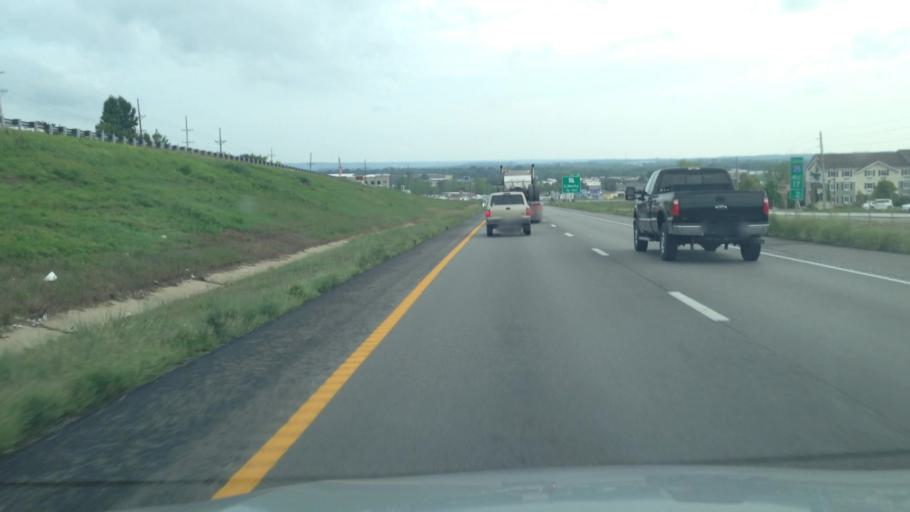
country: US
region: Missouri
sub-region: Clay County
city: Liberty
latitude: 39.2570
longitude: -94.4500
